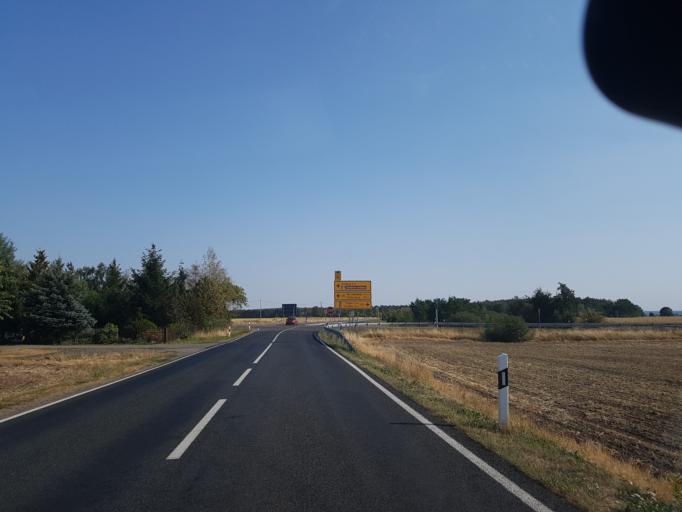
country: DE
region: Saxony
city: Beilrode
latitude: 51.5503
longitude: 13.0854
